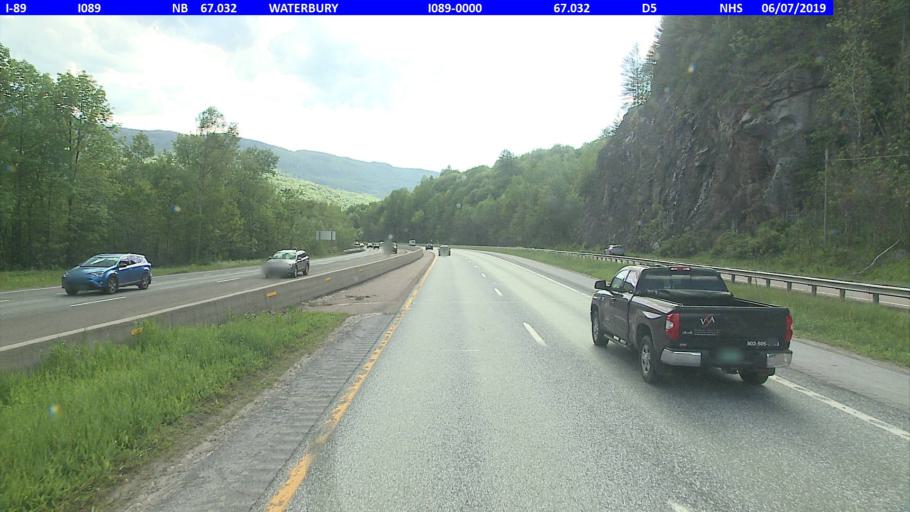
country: US
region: Vermont
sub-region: Washington County
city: Waterbury
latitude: 44.3603
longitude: -72.8093
